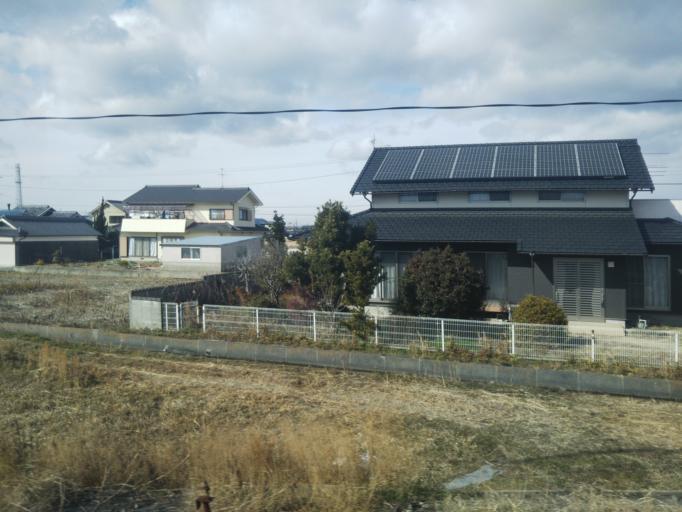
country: JP
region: Okayama
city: Okayama-shi
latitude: 34.6092
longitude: 133.8733
